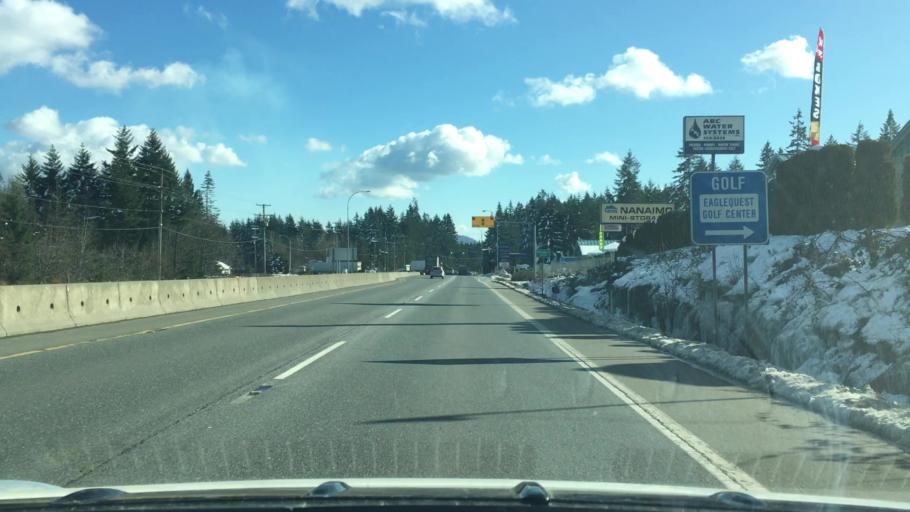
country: CA
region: British Columbia
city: Nanaimo
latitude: 49.0956
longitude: -123.8875
